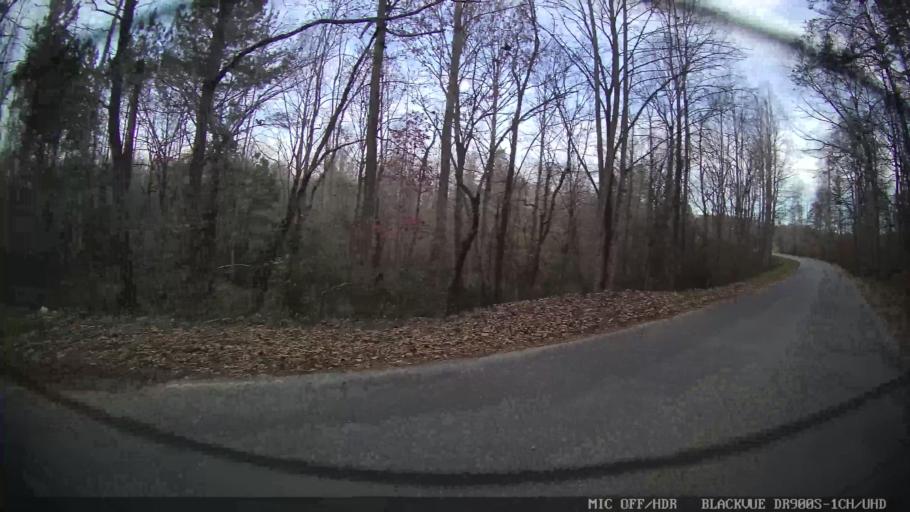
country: US
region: Georgia
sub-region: Union County
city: Blairsville
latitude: 34.9636
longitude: -83.8935
